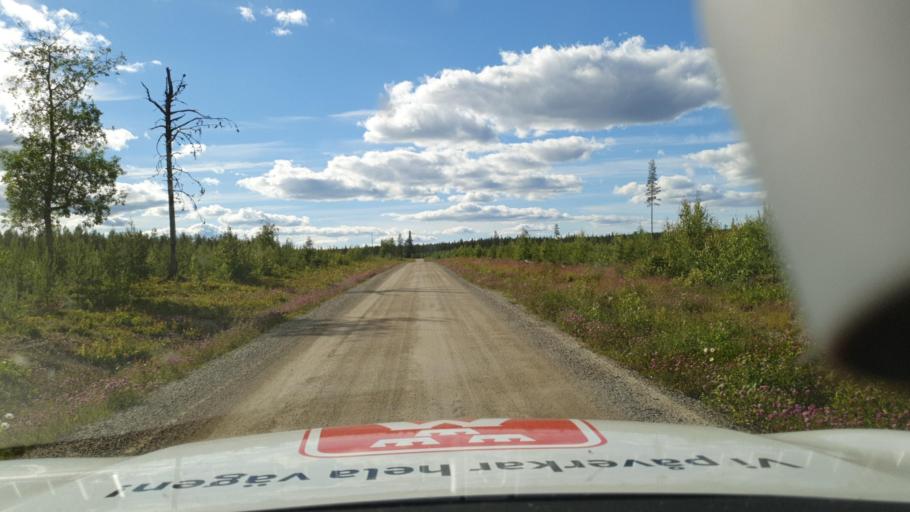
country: SE
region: Vaesterbotten
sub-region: Lycksele Kommun
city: Lycksele
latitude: 64.4021
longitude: 18.5629
